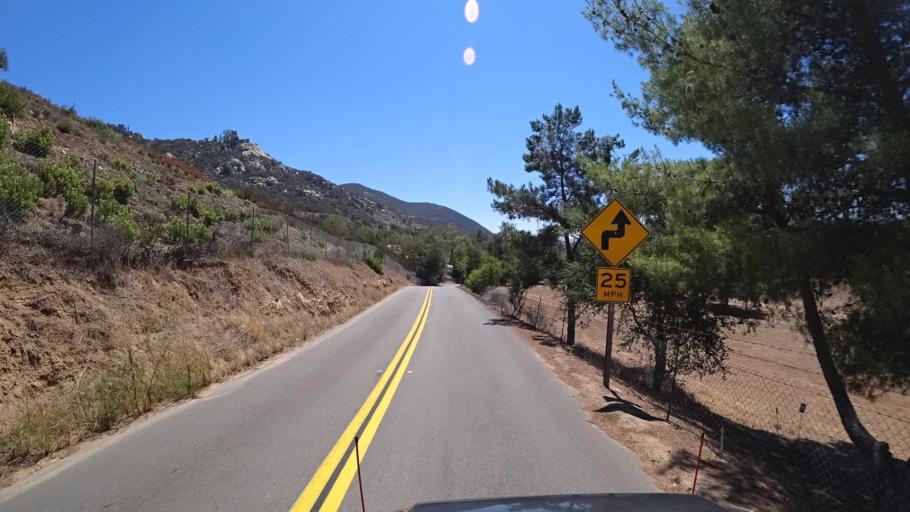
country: US
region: California
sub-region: San Diego County
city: Rainbow
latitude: 33.3876
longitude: -117.1407
